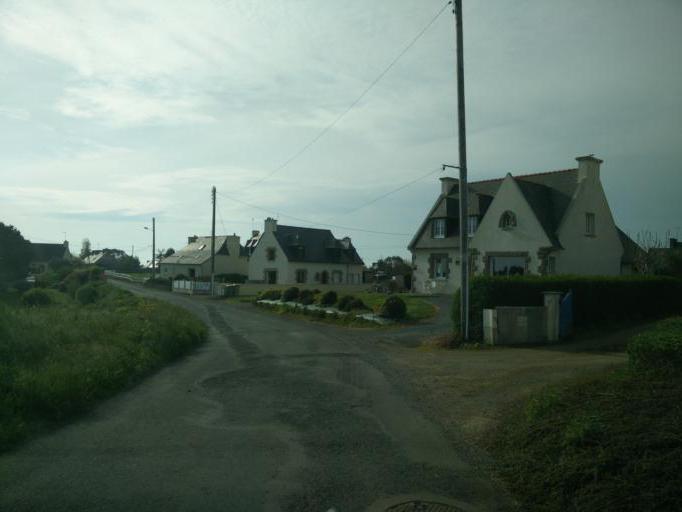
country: FR
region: Brittany
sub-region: Departement des Cotes-d'Armor
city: Pleubian
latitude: 48.8639
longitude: -3.0998
